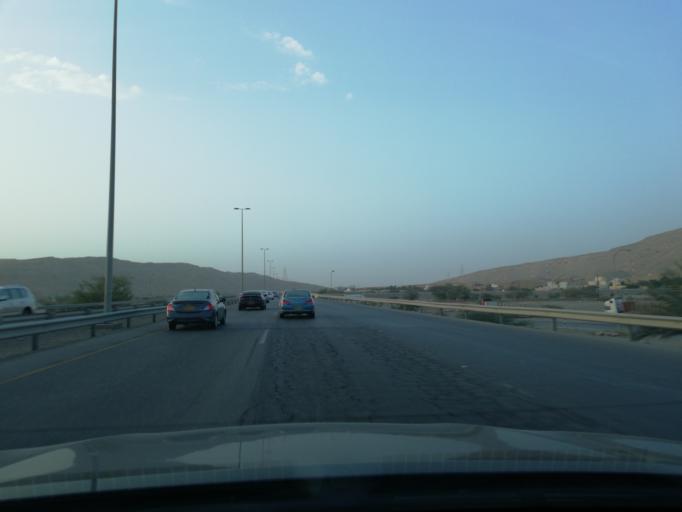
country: OM
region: Muhafazat ad Dakhiliyah
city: Bidbid
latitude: 23.5290
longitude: 58.1886
